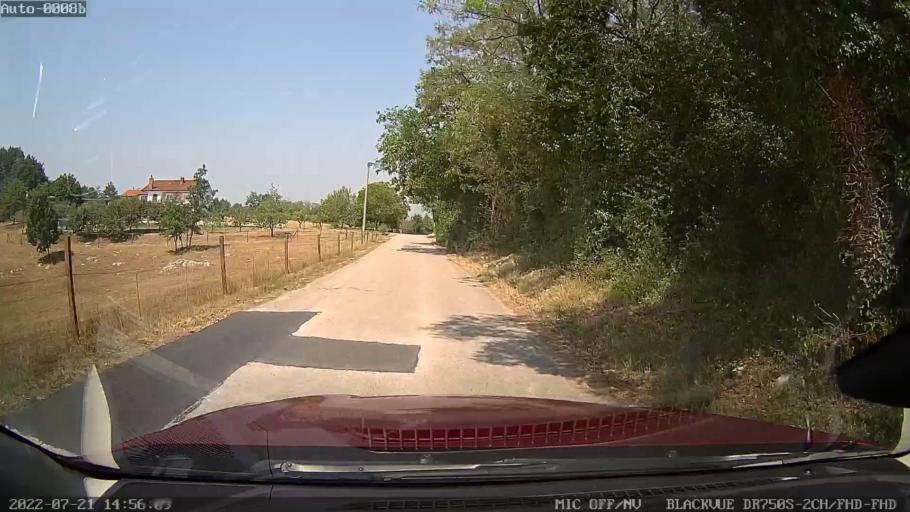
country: HR
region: Istarska
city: Pazin
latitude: 45.1992
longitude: 13.9468
